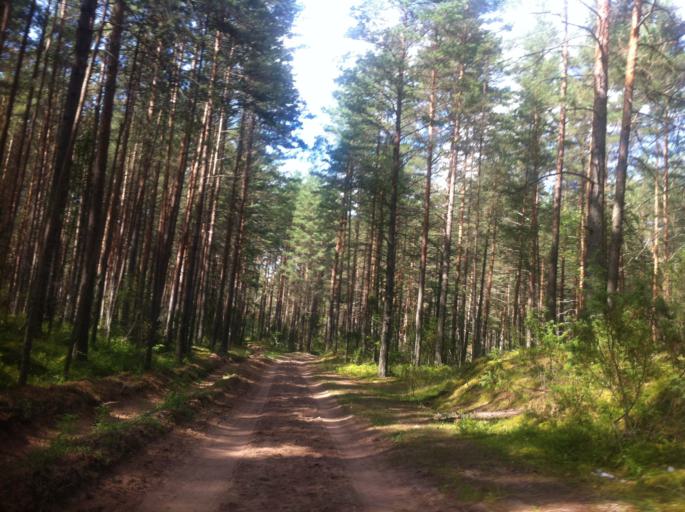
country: RU
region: Pskov
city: Izborsk
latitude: 57.8293
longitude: 27.9380
